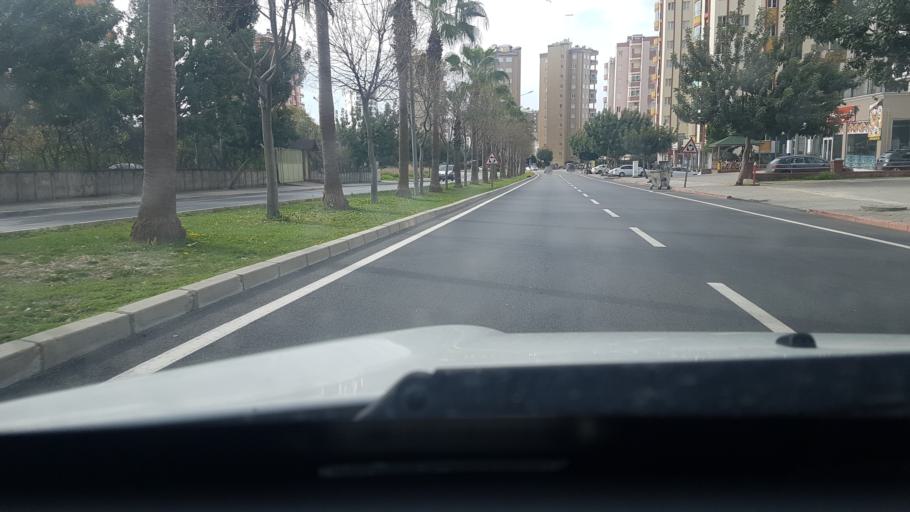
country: TR
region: Adana
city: Seyhan
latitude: 37.0336
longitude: 35.2810
